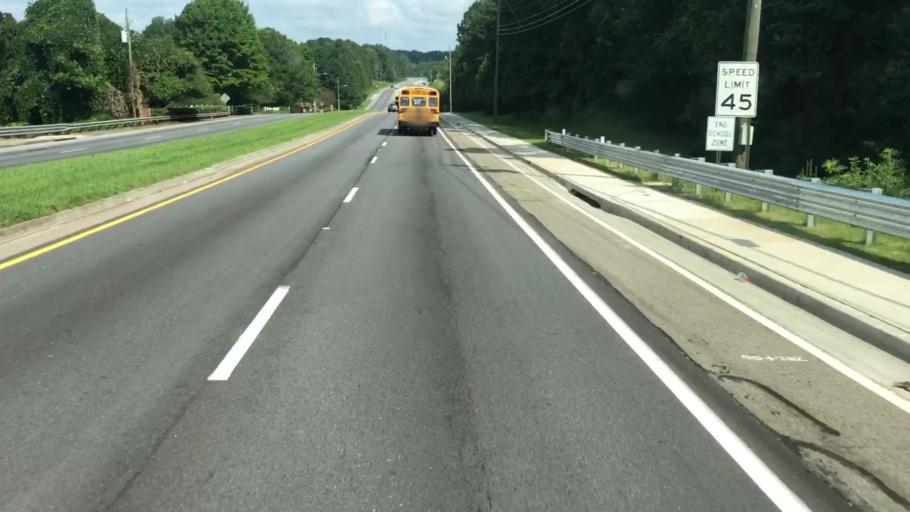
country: US
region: Georgia
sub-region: Gwinnett County
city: Lawrenceville
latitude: 33.9291
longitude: -84.0257
